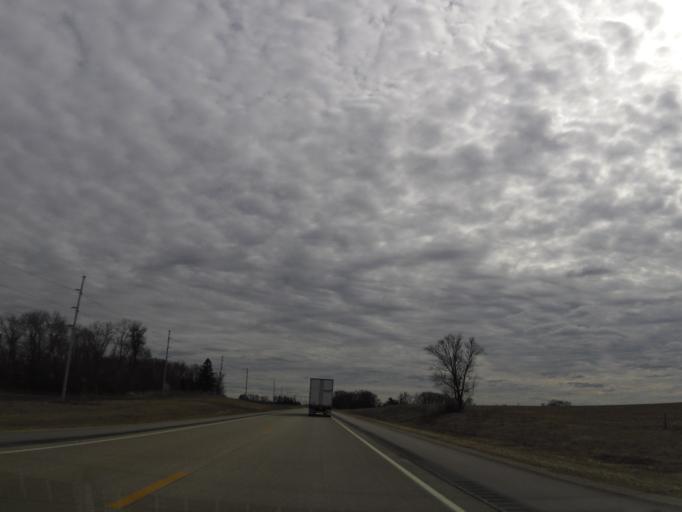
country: US
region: Minnesota
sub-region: Fillmore County
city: Spring Valley
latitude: 43.5793
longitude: -92.3892
